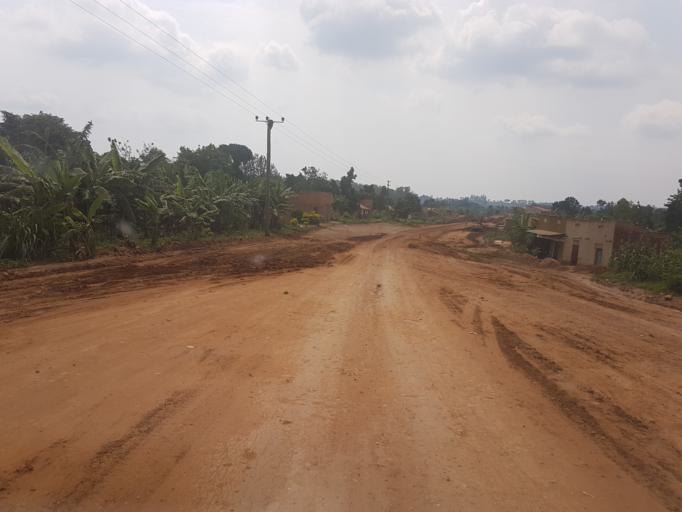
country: UG
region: Western Region
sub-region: Kanungu District
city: Ntungamo
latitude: -0.8043
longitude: 29.7036
